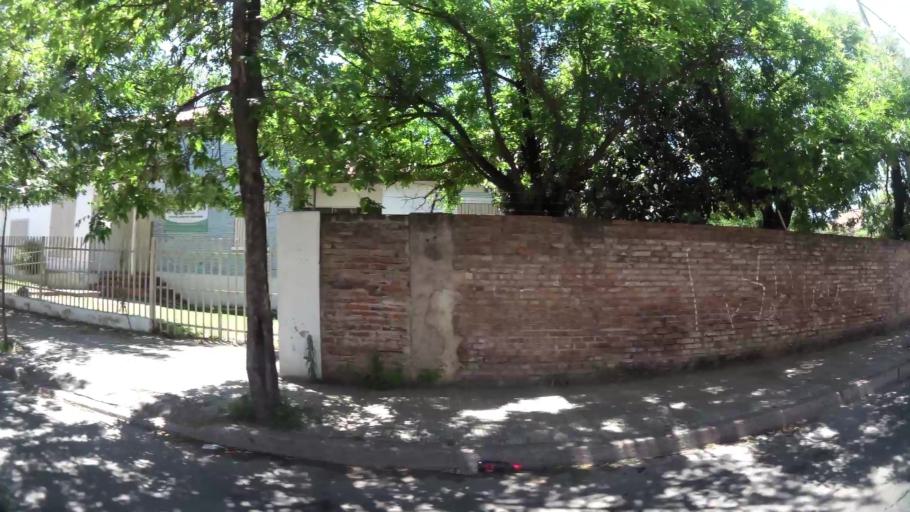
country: AR
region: Cordoba
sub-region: Departamento de Capital
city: Cordoba
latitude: -31.4105
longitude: -64.2059
